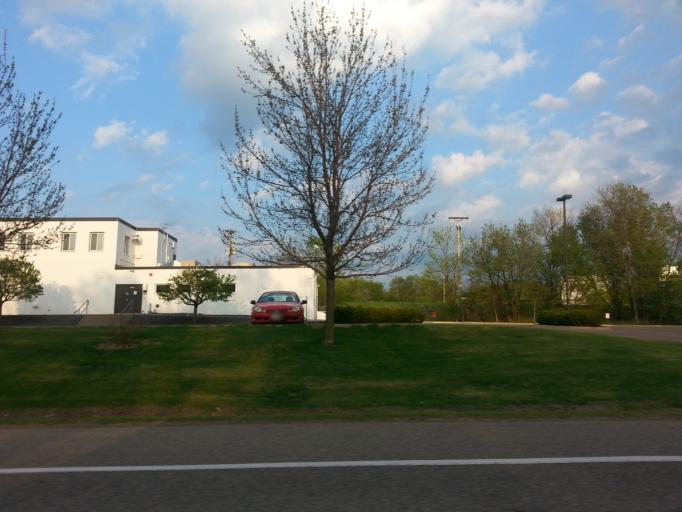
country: US
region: Minnesota
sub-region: Dakota County
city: Mendota Heights
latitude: 44.8679
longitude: -93.1726
